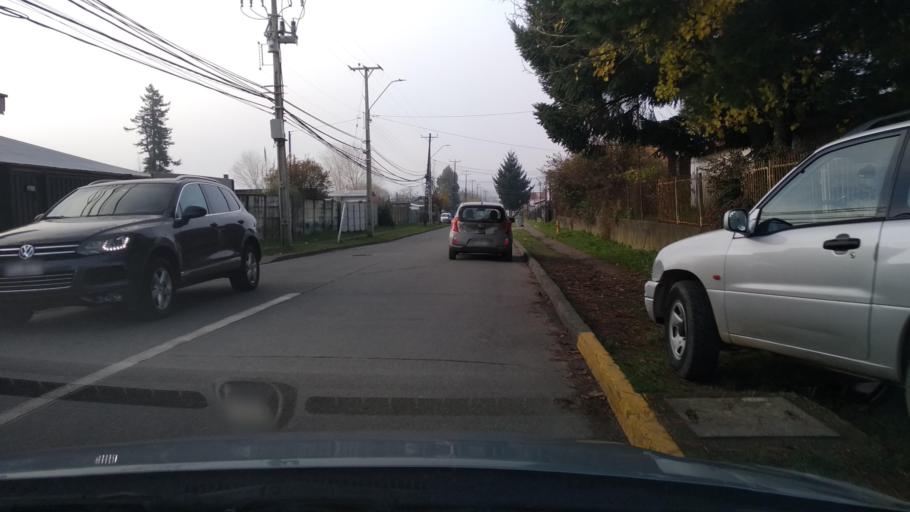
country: CL
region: Los Lagos
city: Las Animas
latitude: -39.8125
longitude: -73.2302
